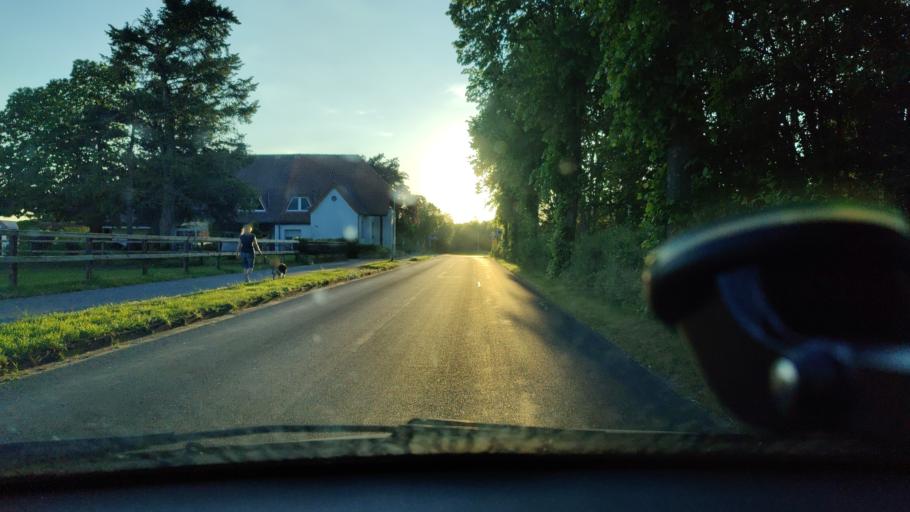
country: DE
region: North Rhine-Westphalia
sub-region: Regierungsbezirk Dusseldorf
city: Kranenburg
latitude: 51.7846
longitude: 6.0126
